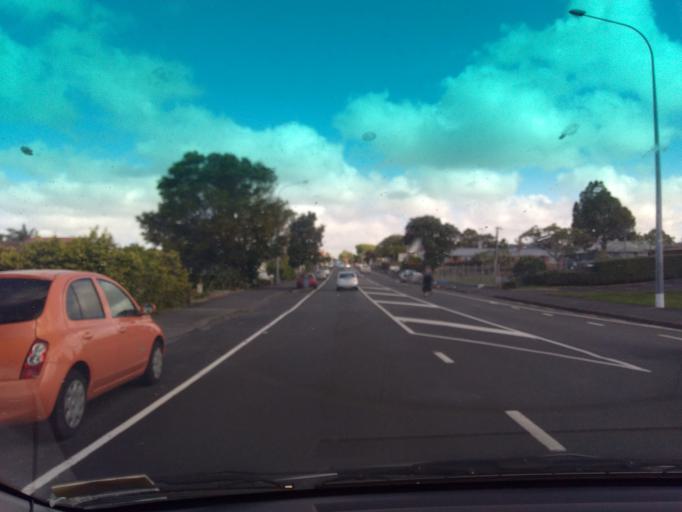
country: NZ
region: Auckland
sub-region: Auckland
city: Rosebank
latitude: -36.8669
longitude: 174.7076
